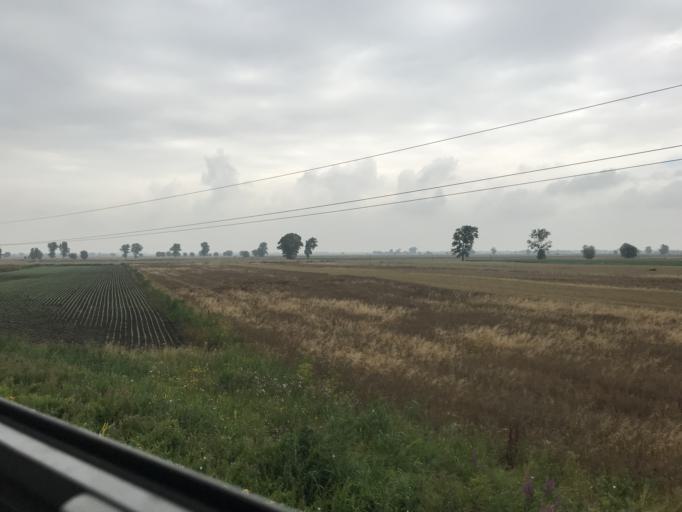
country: PL
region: Pomeranian Voivodeship
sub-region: Powiat tczewski
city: Tczew
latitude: 54.1222
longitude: 18.7656
